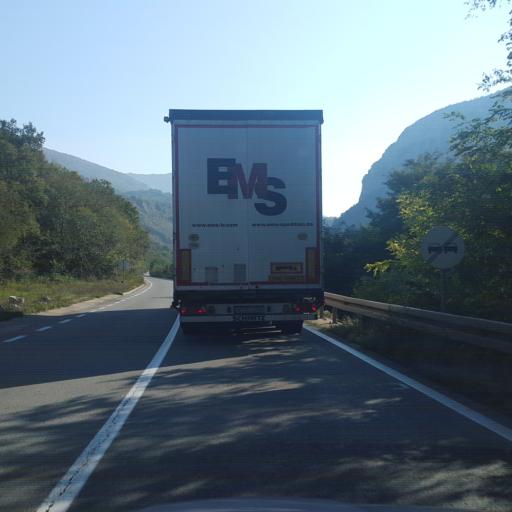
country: RS
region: Central Serbia
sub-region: Nisavski Okrug
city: Niska Banja
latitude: 43.3330
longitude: 22.0736
